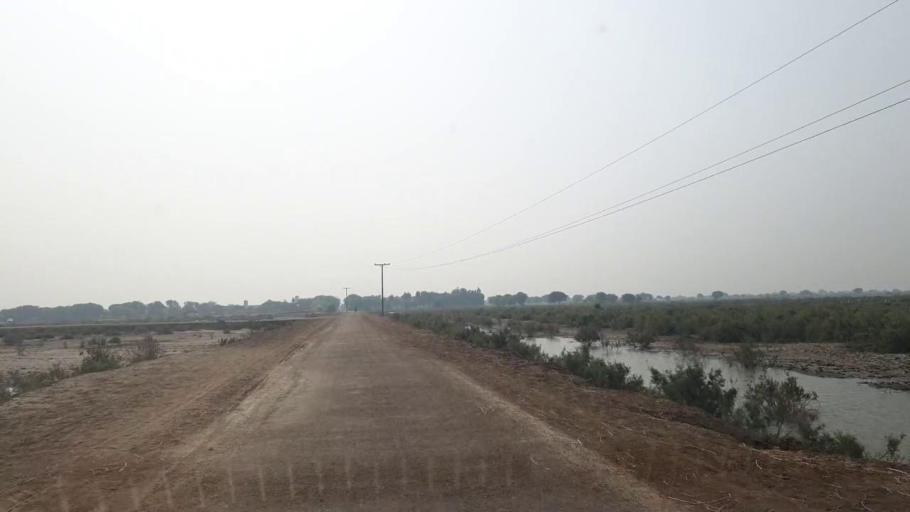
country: PK
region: Sindh
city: Matli
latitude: 25.1314
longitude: 68.6906
